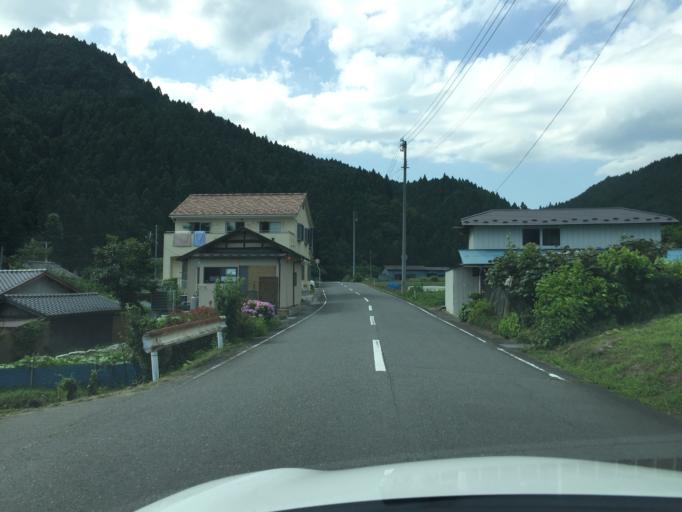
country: JP
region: Fukushima
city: Iwaki
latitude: 37.0242
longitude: 140.7034
